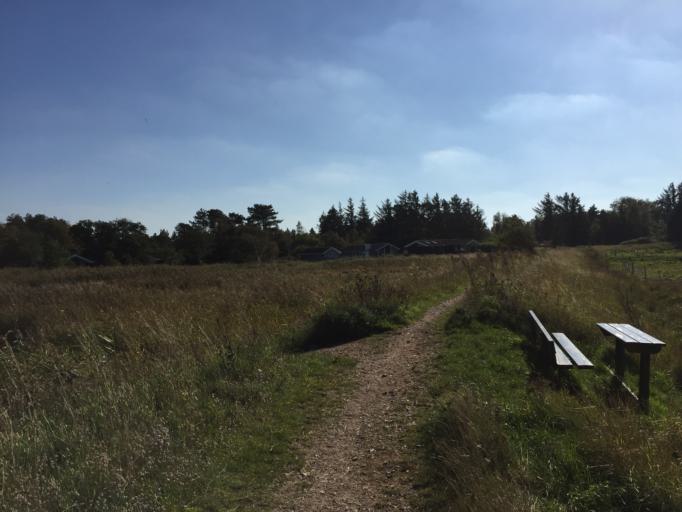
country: DK
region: Zealand
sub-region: Odsherred Kommune
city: Hojby
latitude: 55.8919
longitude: 11.5350
